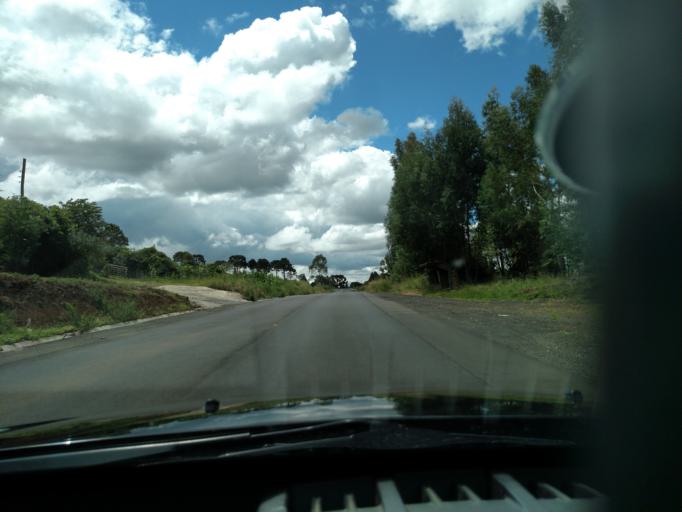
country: BR
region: Santa Catarina
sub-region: Sao Joaquim
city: Sao Joaquim
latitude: -28.2009
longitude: -49.9950
